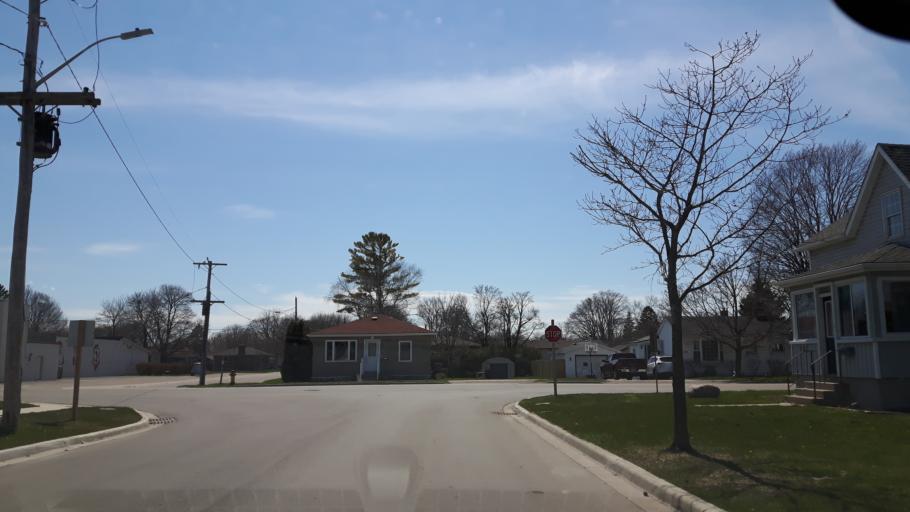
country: CA
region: Ontario
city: Goderich
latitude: 43.7381
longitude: -81.7004
